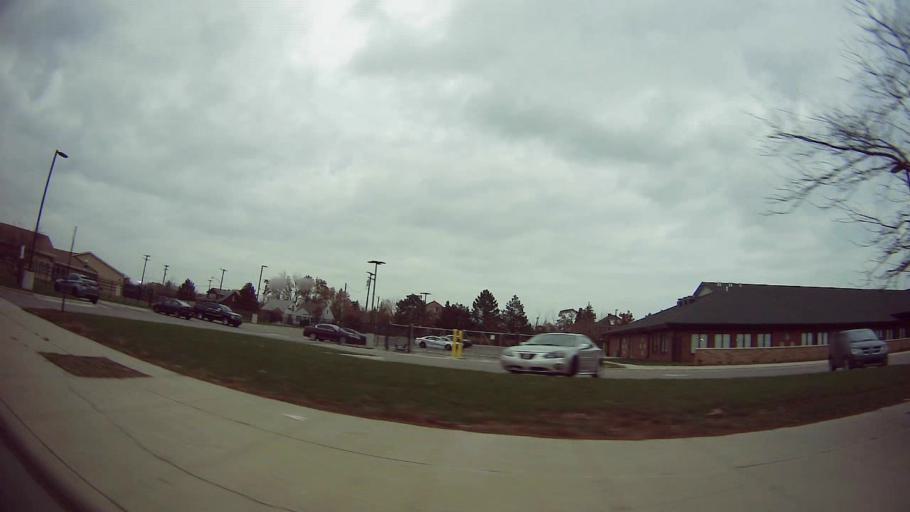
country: US
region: Michigan
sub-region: Wayne County
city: Grosse Pointe Park
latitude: 42.3833
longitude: -82.9674
